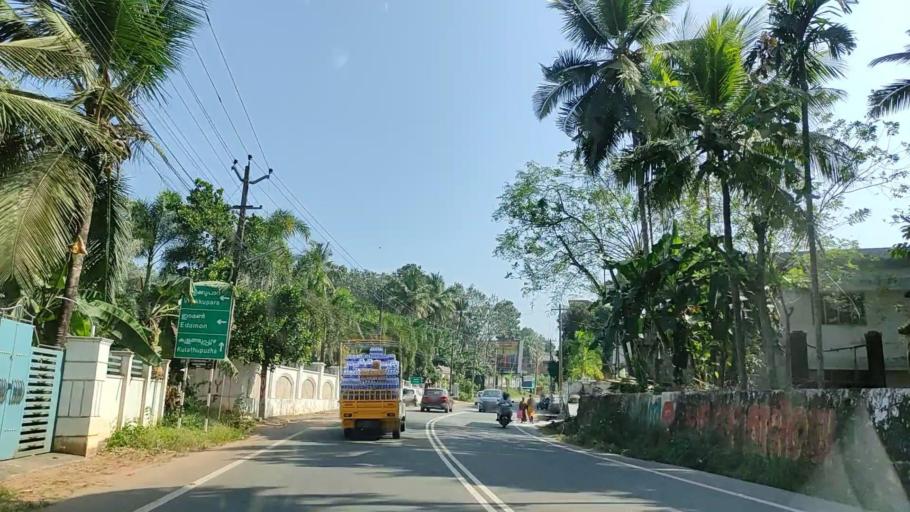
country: IN
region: Kerala
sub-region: Kollam
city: Punalur
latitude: 8.9354
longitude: 76.9444
